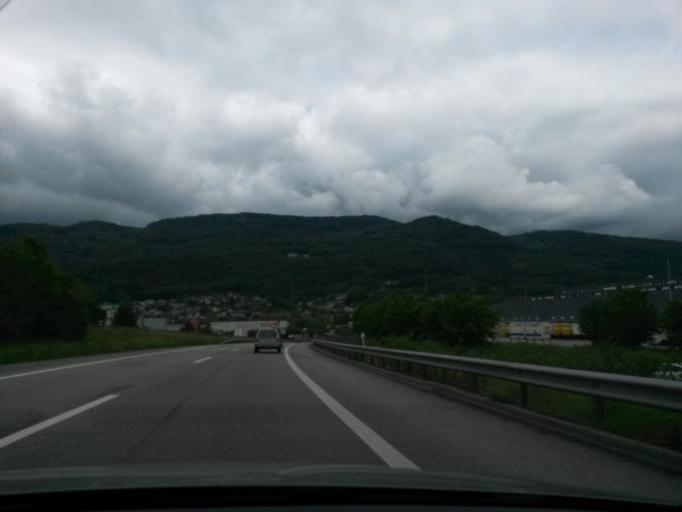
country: CH
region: Solothurn
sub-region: Bezirk Olten
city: Gunzgen
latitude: 47.3140
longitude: 7.8074
